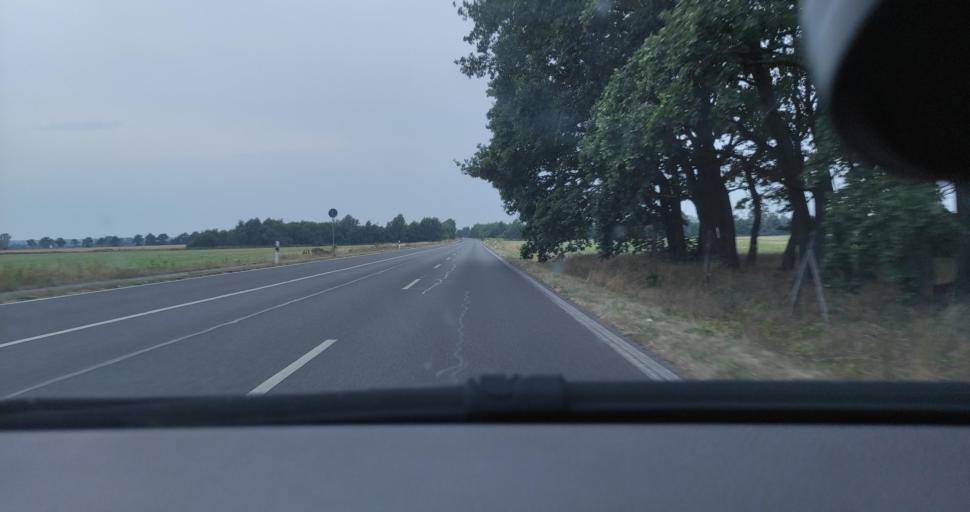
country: DE
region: Brandenburg
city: Forst
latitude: 51.7672
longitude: 14.6441
